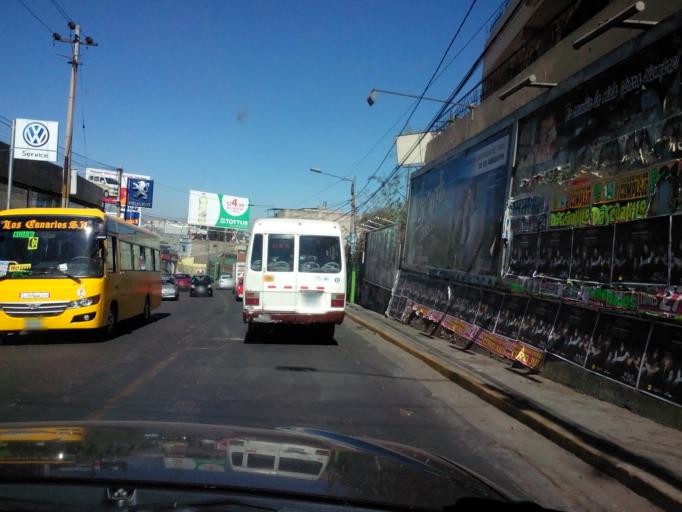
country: PE
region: Arequipa
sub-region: Provincia de Arequipa
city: Arequipa
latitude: -16.3875
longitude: -71.5530
